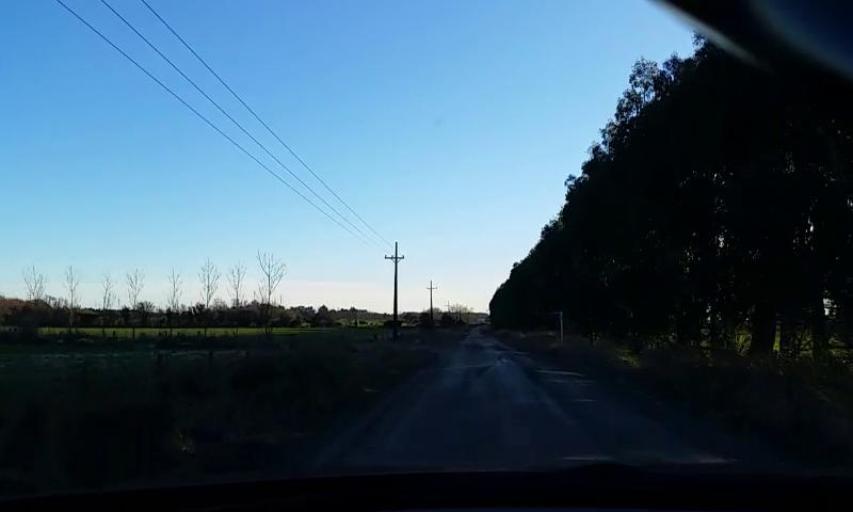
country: NZ
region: Southland
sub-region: Invercargill City
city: Invercargill
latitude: -46.2918
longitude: 168.4382
